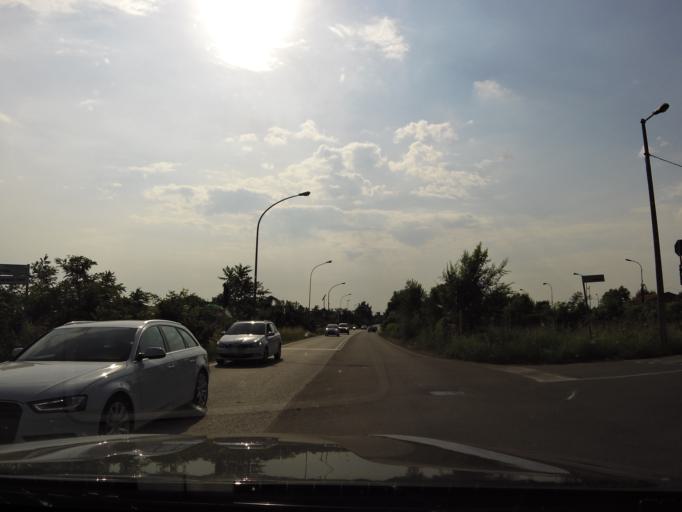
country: IT
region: Veneto
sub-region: Provincia di Verona
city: Parona
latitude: 45.4491
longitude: 10.9397
